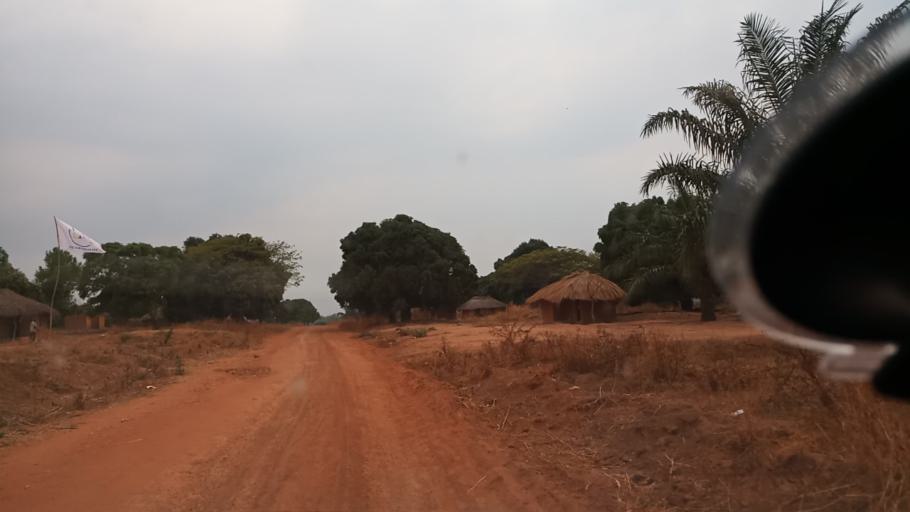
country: ZM
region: Luapula
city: Nchelenge
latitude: -9.0653
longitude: 28.3558
